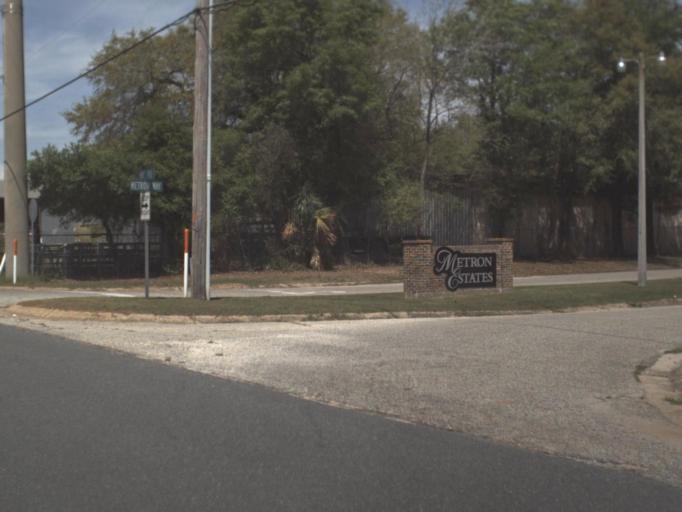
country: US
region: Florida
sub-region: Santa Rosa County
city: Pace
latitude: 30.6033
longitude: -87.1099
